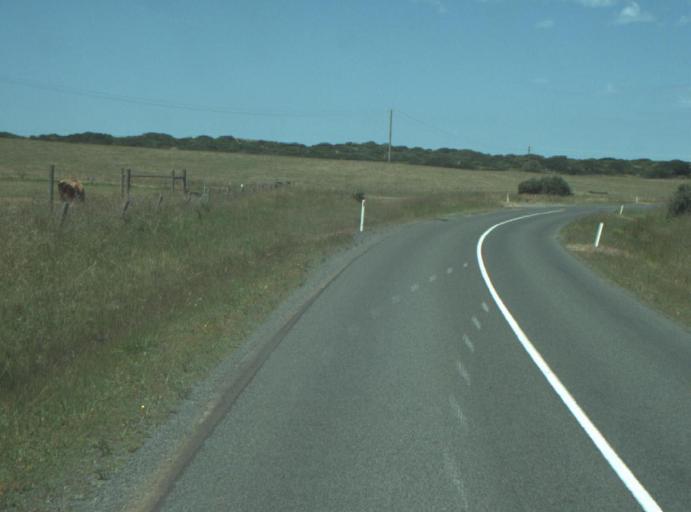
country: AU
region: Victoria
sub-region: Greater Geelong
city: Leopold
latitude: -38.2744
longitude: 144.4367
